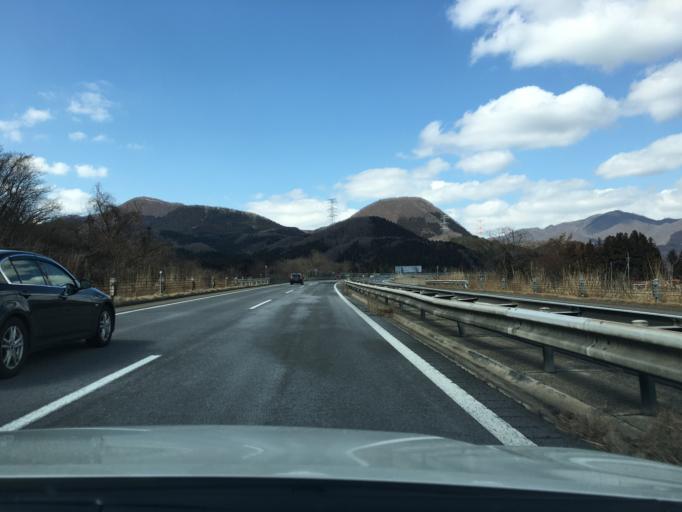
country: JP
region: Miyagi
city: Shiroishi
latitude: 38.1836
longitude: 140.6028
